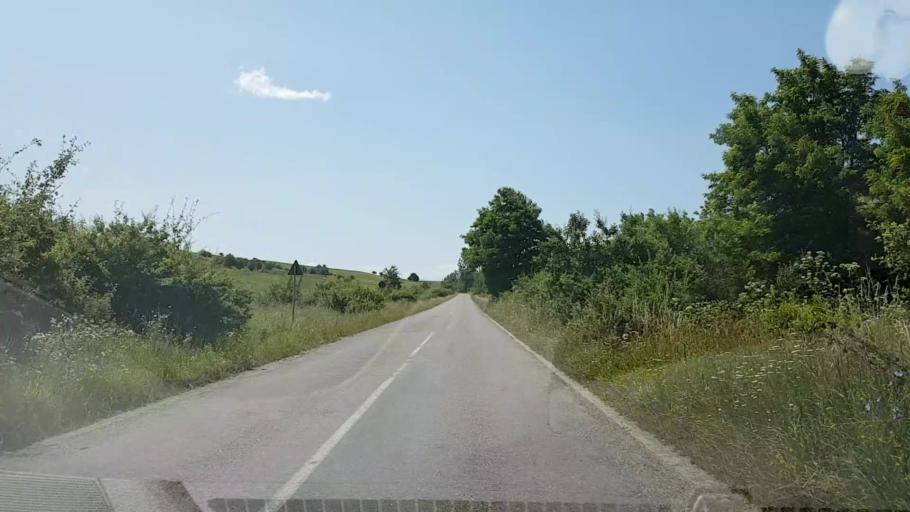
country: RO
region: Brasov
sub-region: Comuna Cincu
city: Cincu
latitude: 45.9486
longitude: 24.7827
